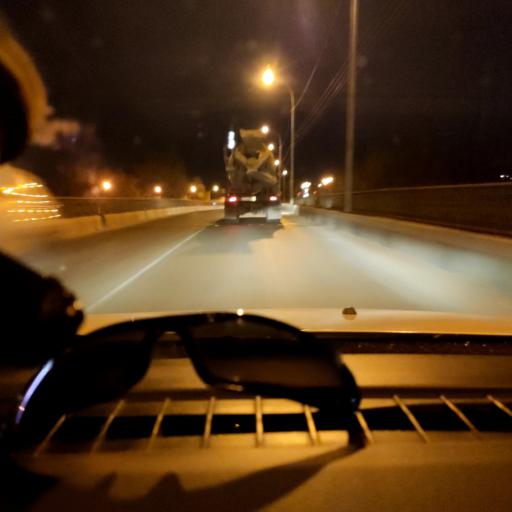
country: RU
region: Samara
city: Novokuybyshevsk
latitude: 53.1152
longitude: 50.0628
